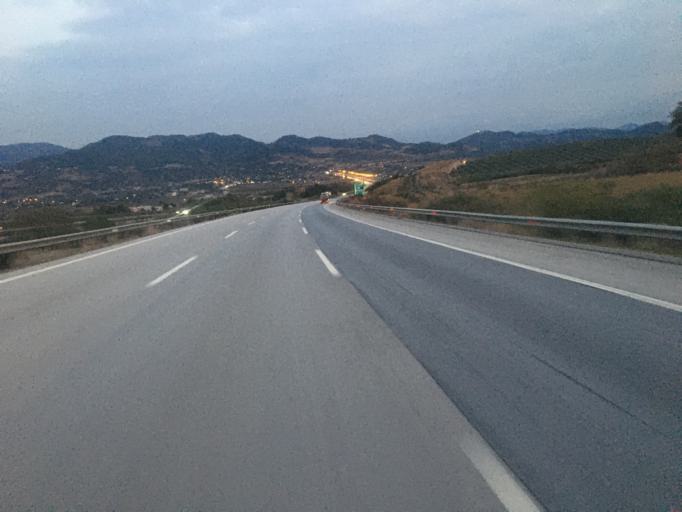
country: TR
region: Osmaniye
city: Haruniye
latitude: 37.2009
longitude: 36.3985
